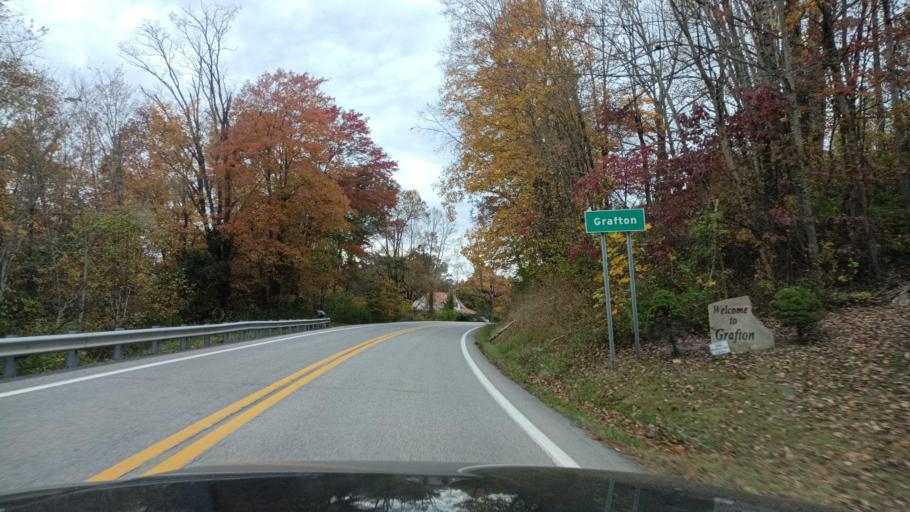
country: US
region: West Virginia
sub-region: Taylor County
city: Grafton
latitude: 39.3426
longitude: -79.9969
